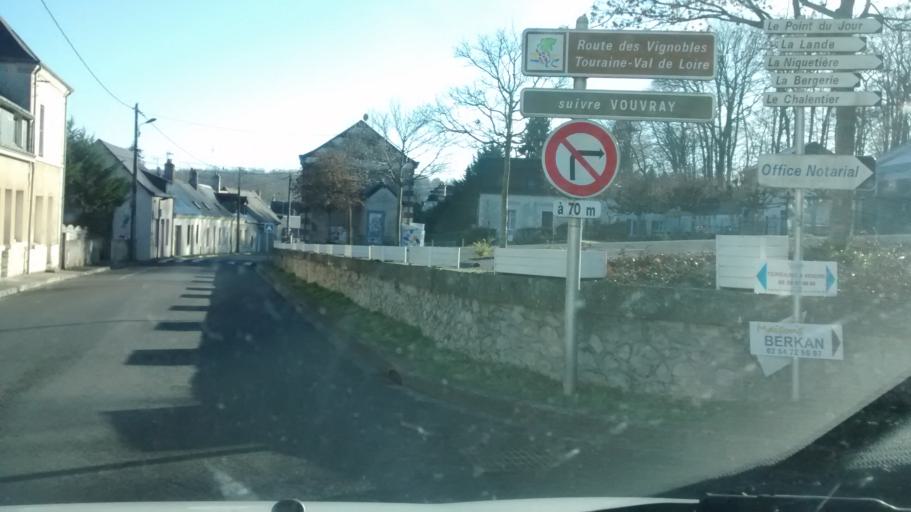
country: FR
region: Centre
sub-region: Departement d'Indre-et-Loire
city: Reugny
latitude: 47.4825
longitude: 0.8814
